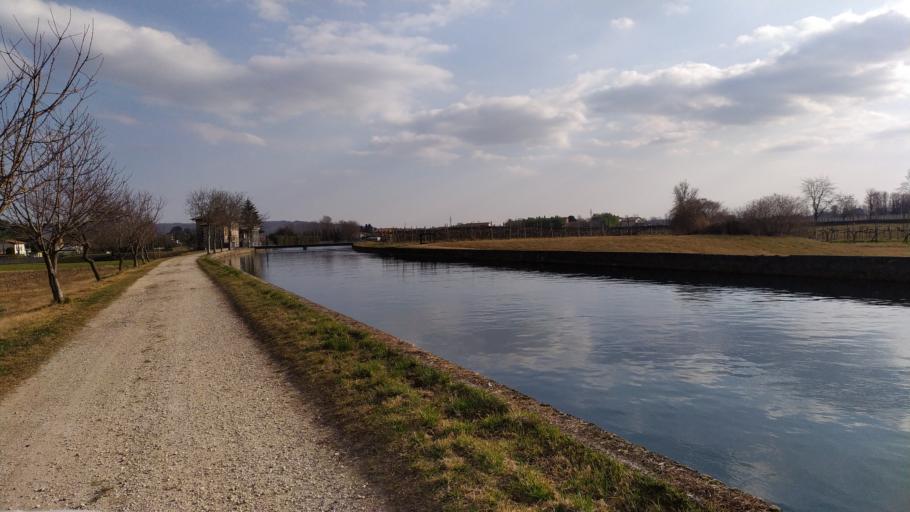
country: IT
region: Veneto
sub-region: Provincia di Treviso
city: Crocetta del Montello
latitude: 45.8434
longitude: 12.0224
